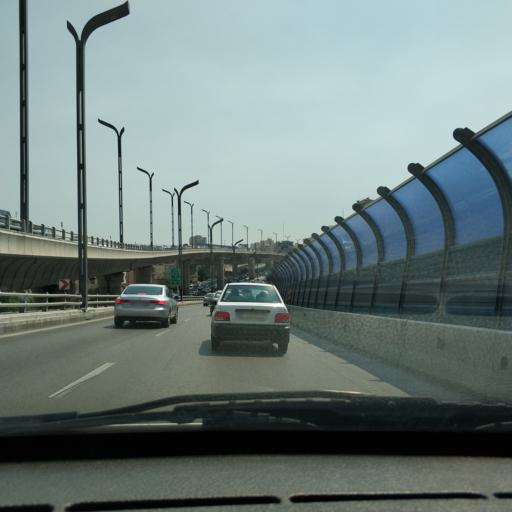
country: IR
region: Tehran
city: Tajrish
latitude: 35.7817
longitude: 51.4335
